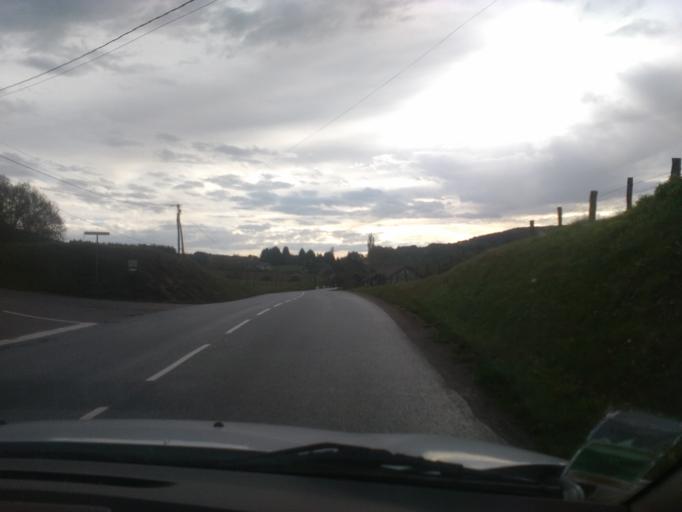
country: FR
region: Lorraine
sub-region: Departement des Vosges
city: Granges-sur-Vologne
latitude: 48.1807
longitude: 6.8120
